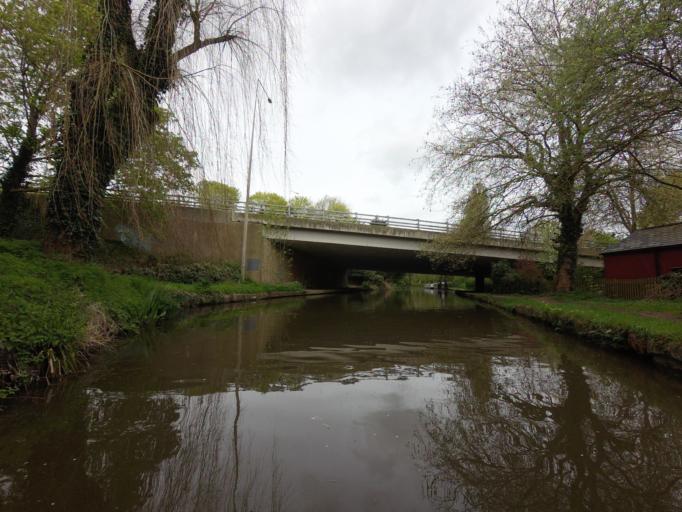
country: GB
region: England
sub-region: Milton Keynes
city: Simpson
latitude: 52.0183
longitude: -0.7182
